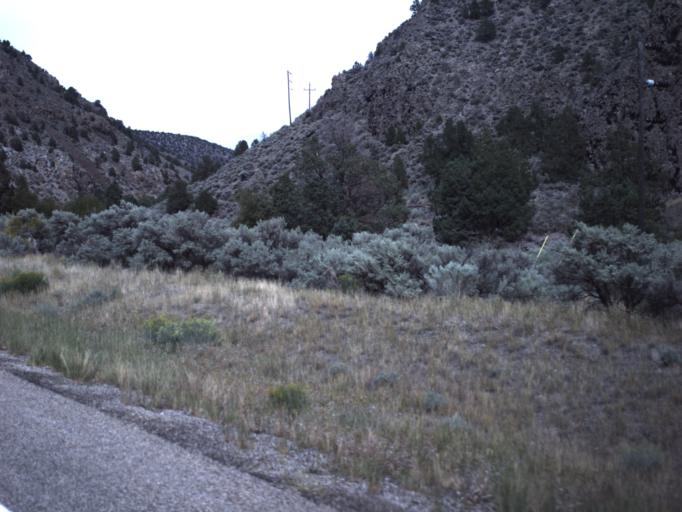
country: US
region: Utah
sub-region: Piute County
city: Junction
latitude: 38.1159
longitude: -112.3382
